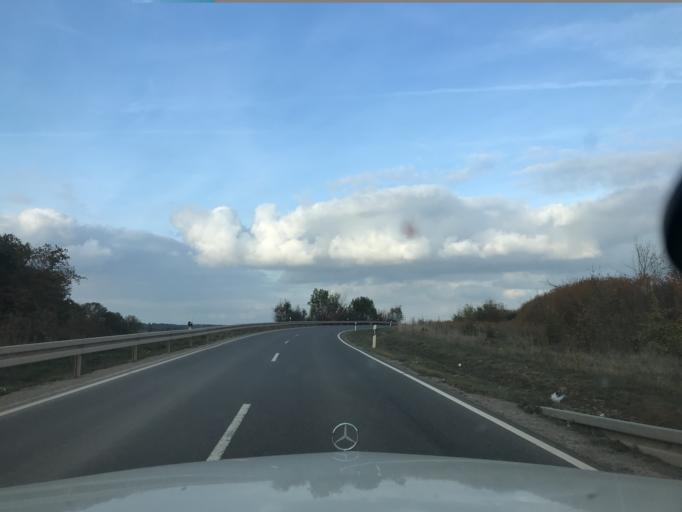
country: DE
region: Hesse
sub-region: Regierungsbezirk Kassel
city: Calden
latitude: 51.4247
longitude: 9.3709
